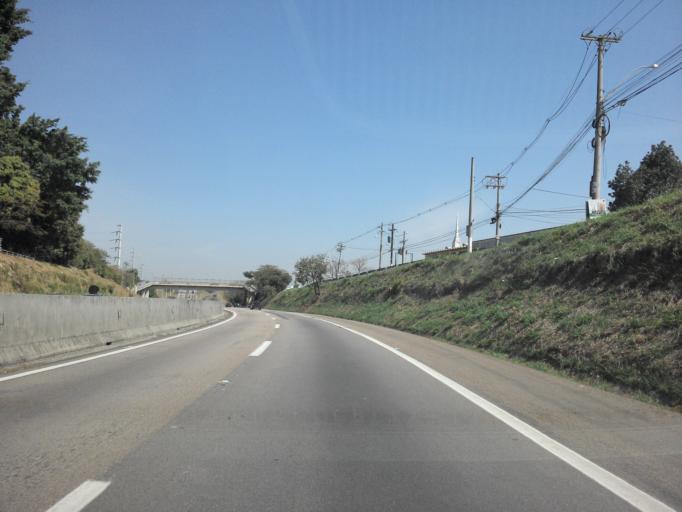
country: BR
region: Sao Paulo
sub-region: Hortolandia
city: Hortolandia
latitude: -22.8927
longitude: -47.1779
